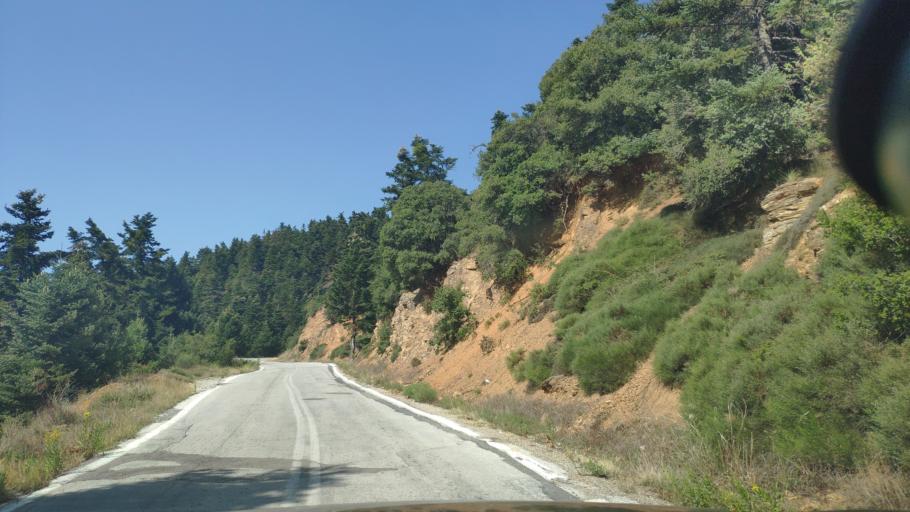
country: GR
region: West Greece
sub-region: Nomos Achaias
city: Aiyira
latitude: 37.8655
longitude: 22.3725
